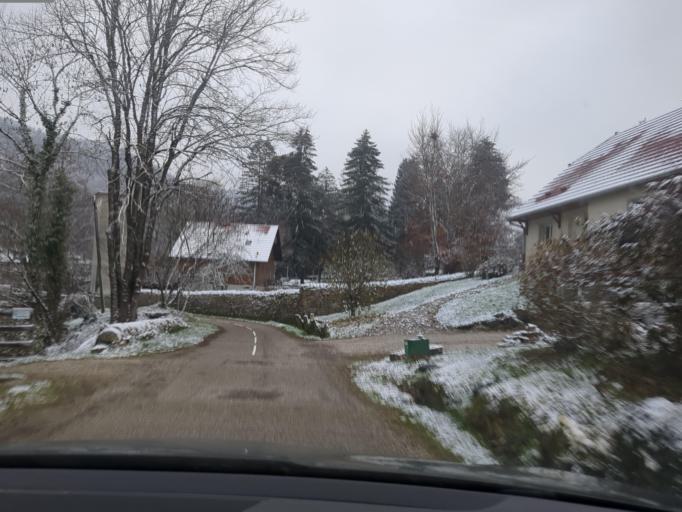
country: FR
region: Franche-Comte
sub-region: Departement du Jura
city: Perrigny
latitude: 46.6545
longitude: 5.5964
